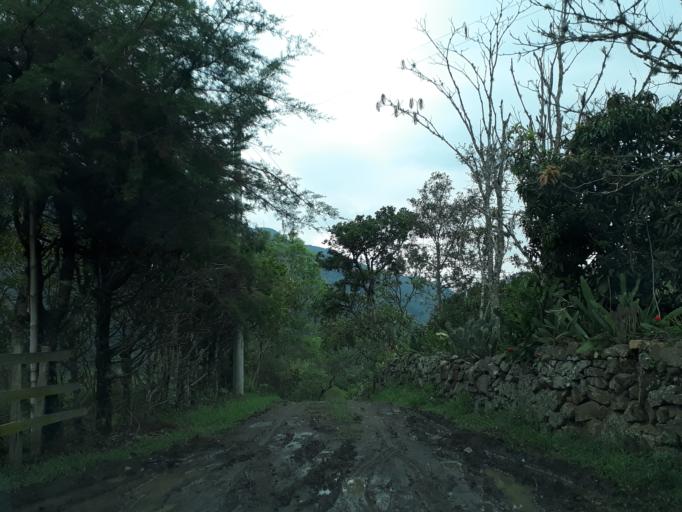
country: CO
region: Cundinamarca
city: Manta
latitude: 5.0597
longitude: -73.5214
